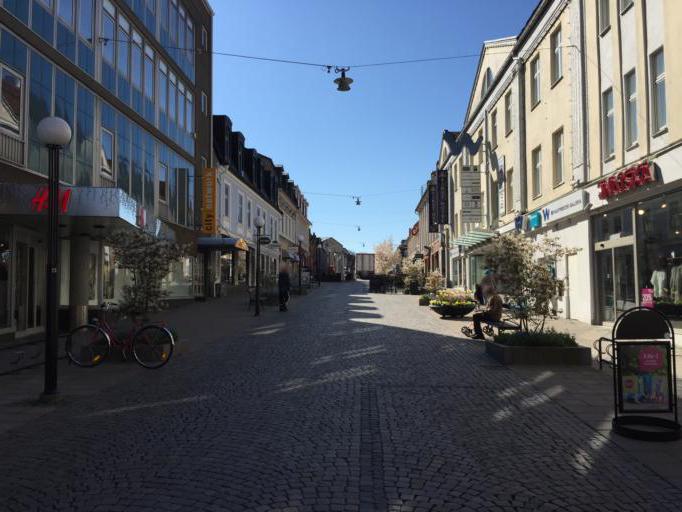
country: SE
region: Blekinge
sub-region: Karlskrona Kommun
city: Karlskrona
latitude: 56.1618
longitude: 15.5836
